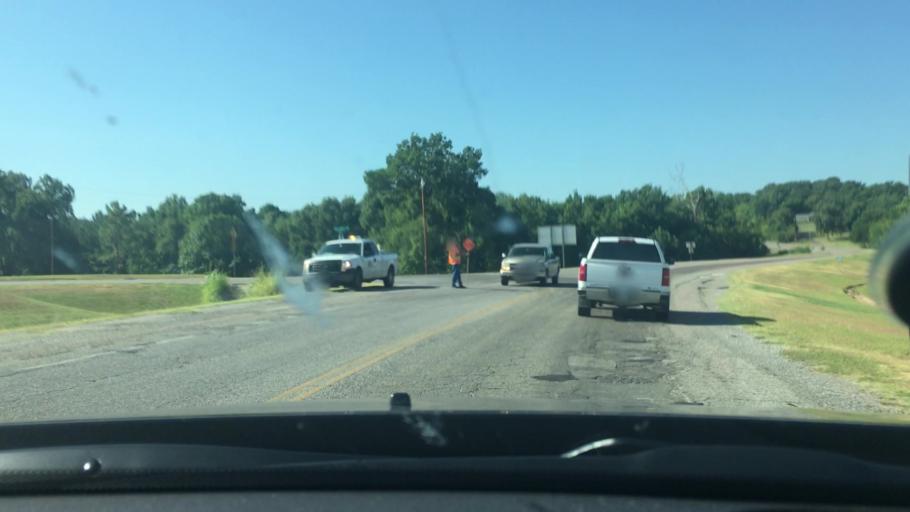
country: US
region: Oklahoma
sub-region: Bryan County
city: Durant
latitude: 34.0186
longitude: -96.3894
